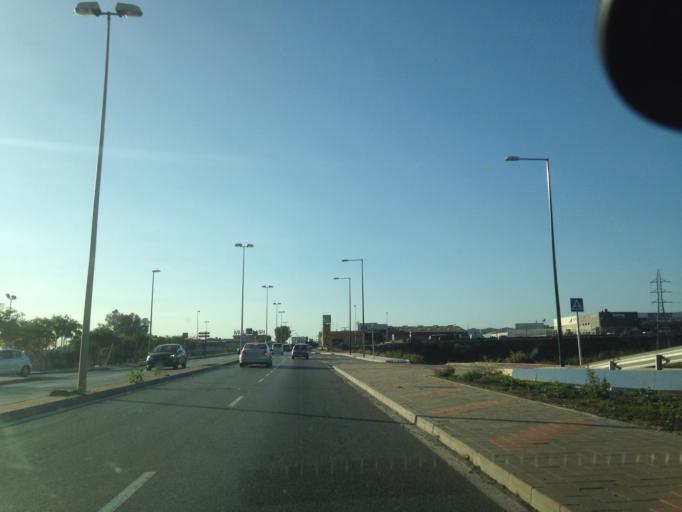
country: ES
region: Andalusia
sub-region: Provincia de Malaga
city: Malaga
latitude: 36.7160
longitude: -4.4831
